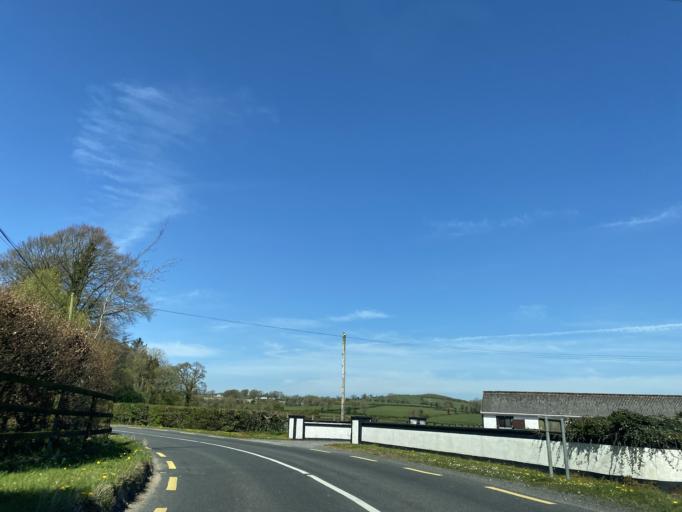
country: IE
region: Leinster
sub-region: Kildare
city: Kildare
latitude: 53.1905
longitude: -6.9022
